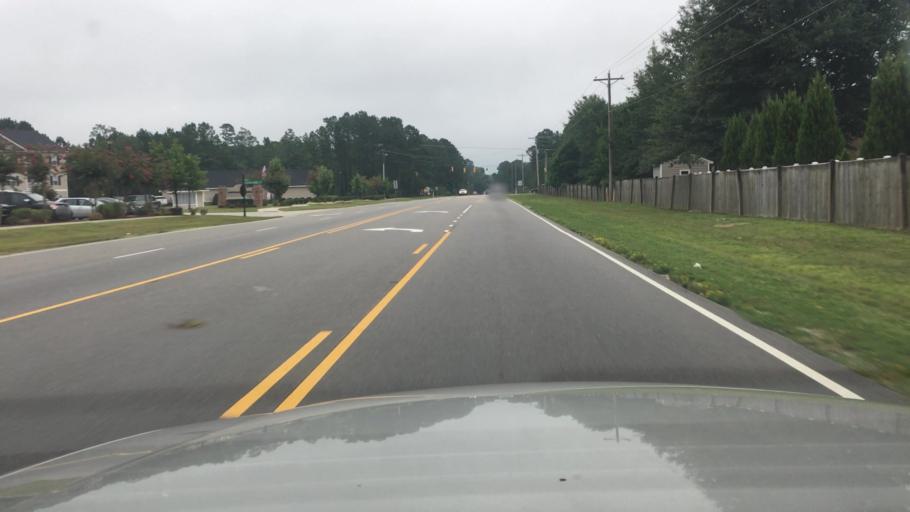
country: US
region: North Carolina
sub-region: Hoke County
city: Rockfish
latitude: 34.9728
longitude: -79.0104
